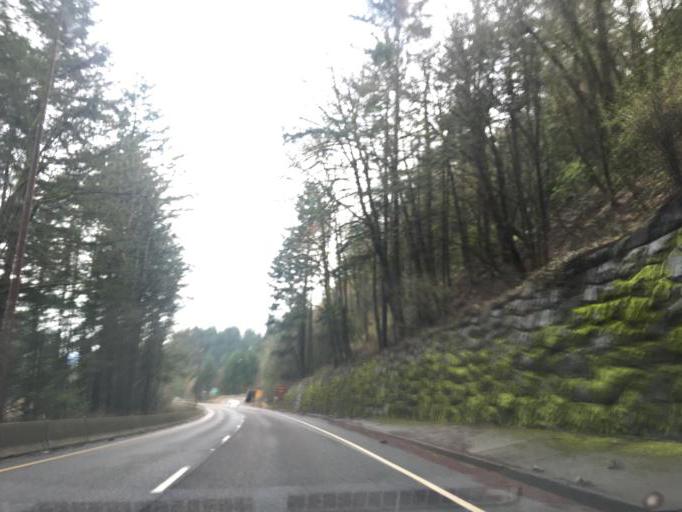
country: US
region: Oregon
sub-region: Hood River County
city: Cascade Locks
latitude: 45.6380
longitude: -121.9367
